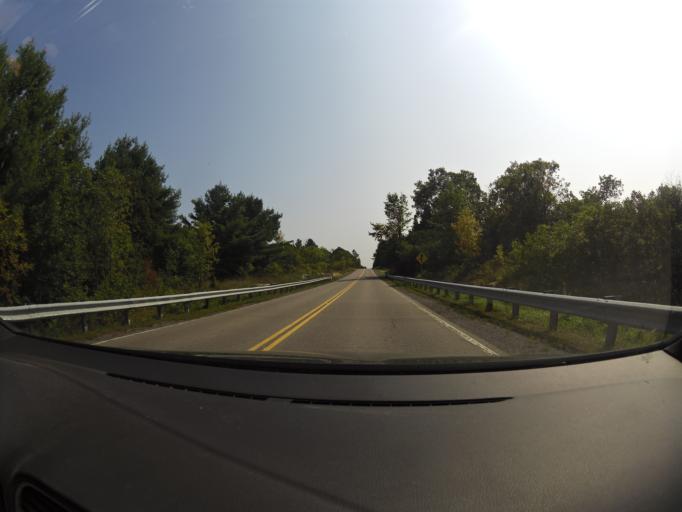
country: CA
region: Ontario
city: Arnprior
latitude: 45.4381
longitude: -76.1775
